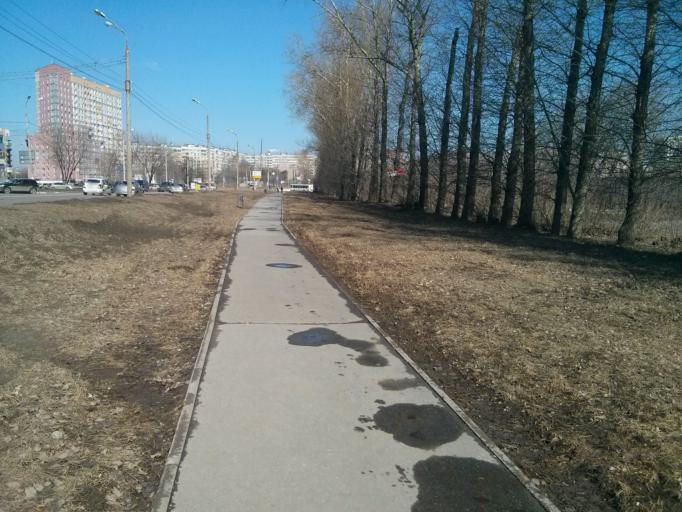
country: RU
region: Nizjnij Novgorod
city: Afonino
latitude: 56.2889
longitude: 44.0760
